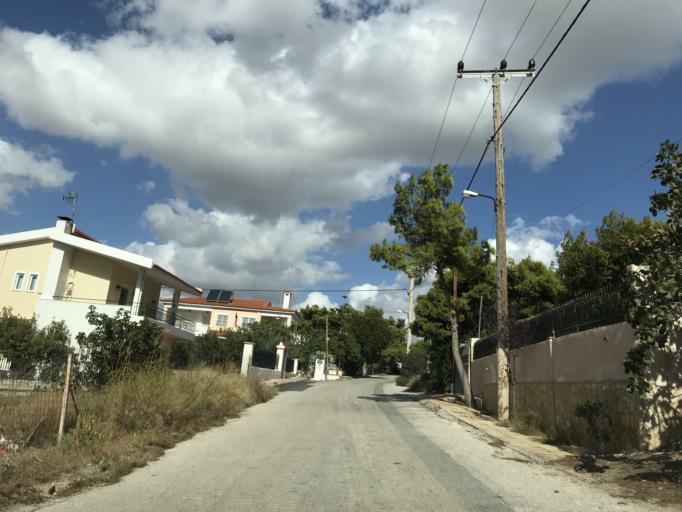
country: GR
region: Attica
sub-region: Nomarchia Anatolikis Attikis
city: Agia Marina
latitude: 37.8174
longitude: 23.8478
